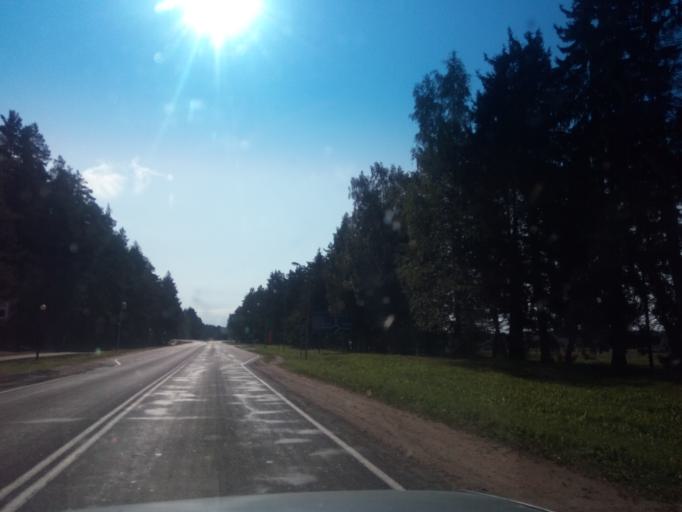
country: BY
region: Vitebsk
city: Vyerkhnyadzvinsk
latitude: 55.7565
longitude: 27.9539
